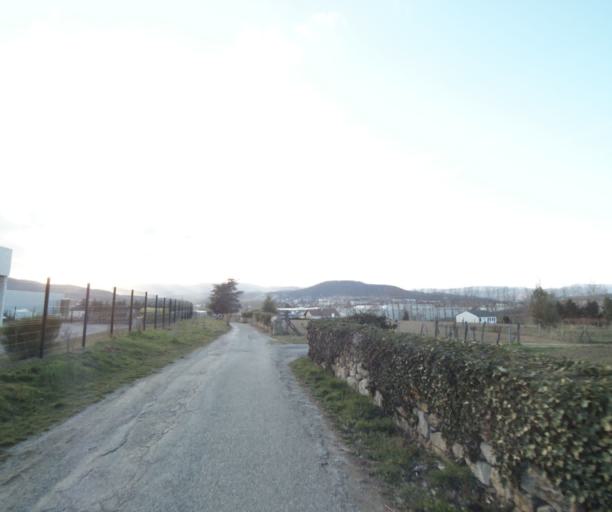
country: FR
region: Rhone-Alpes
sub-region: Departement de l'Ardeche
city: Davezieux
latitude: 45.2421
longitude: 4.6956
